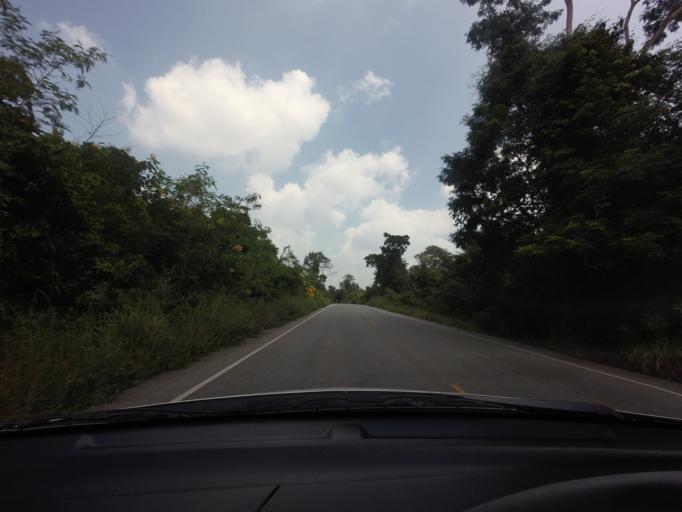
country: TH
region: Nakhon Ratchasima
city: Pak Chong
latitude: 14.6073
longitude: 101.5762
